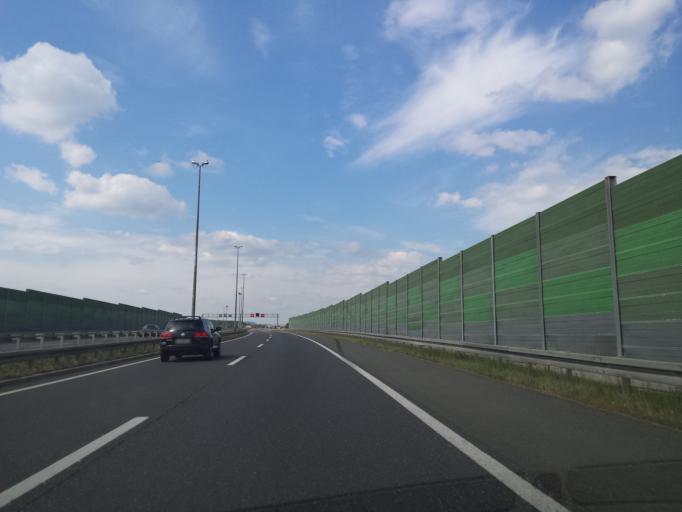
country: HR
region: Grad Zagreb
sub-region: Sesvete
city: Sesvete
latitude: 45.8153
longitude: 16.1375
